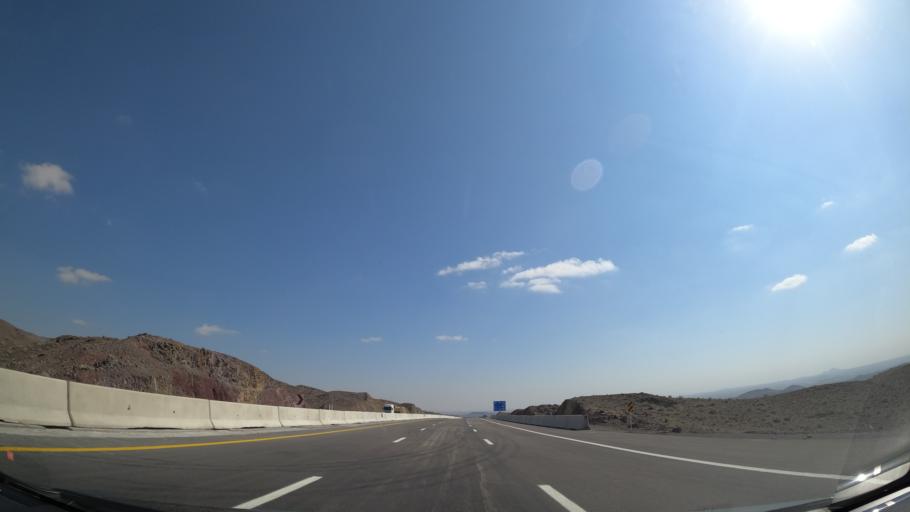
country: IR
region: Alborz
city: Nazarabad
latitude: 35.6583
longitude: 50.6616
